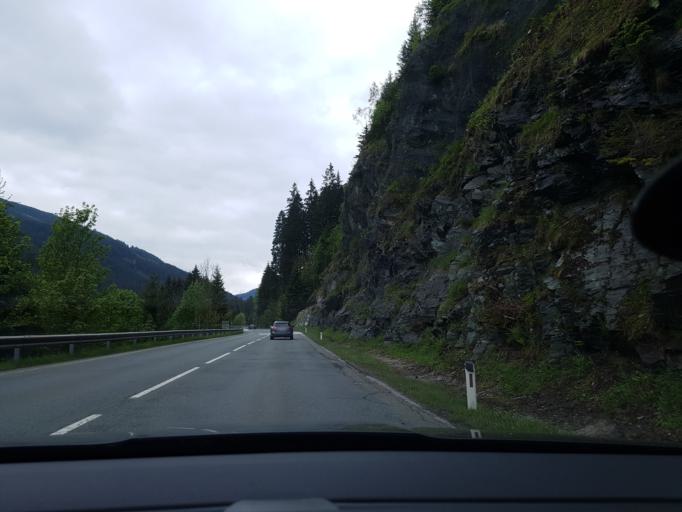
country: AT
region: Tyrol
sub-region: Politischer Bezirk Kitzbuhel
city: Jochberg
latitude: 47.3535
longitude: 12.4140
